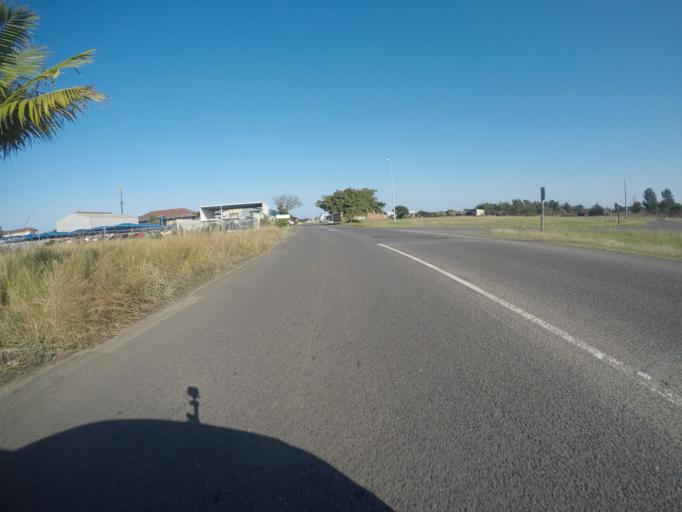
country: ZA
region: KwaZulu-Natal
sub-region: uThungulu District Municipality
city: Richards Bay
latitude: -28.7918
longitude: 32.0775
